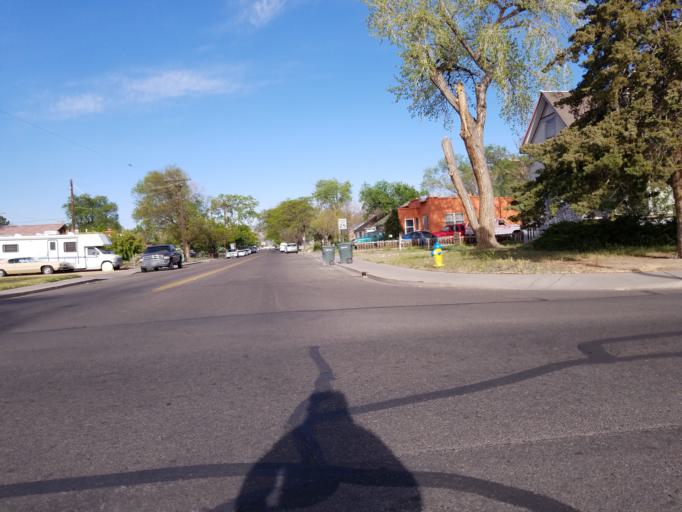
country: US
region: Colorado
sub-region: Mesa County
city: Grand Junction
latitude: 39.0810
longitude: -108.5477
